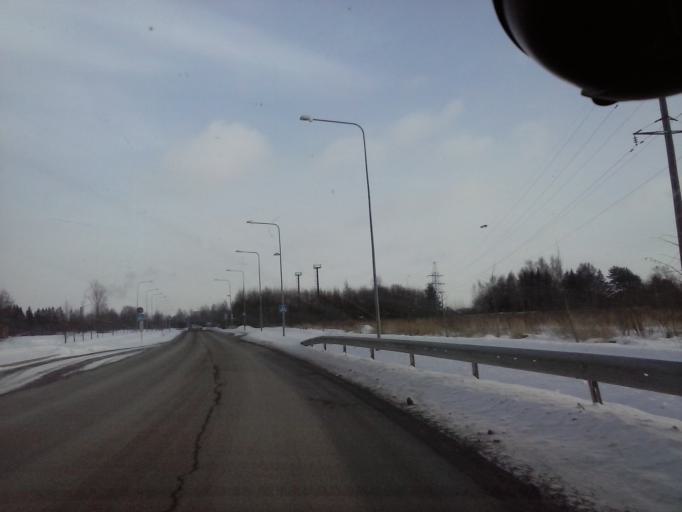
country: EE
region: Tartu
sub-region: Tartu linn
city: Tartu
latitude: 58.3563
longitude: 26.6722
